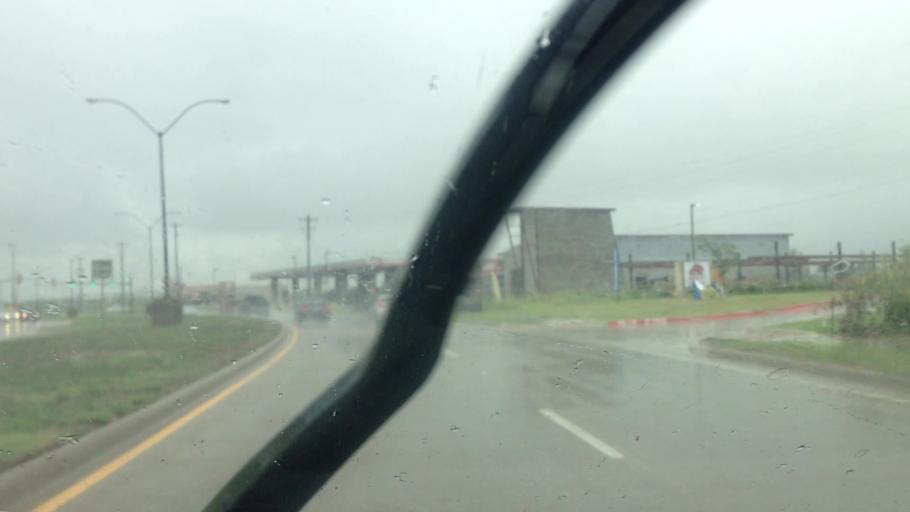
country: US
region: Texas
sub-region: Tarrant County
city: Haslet
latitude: 32.9332
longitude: -97.3098
